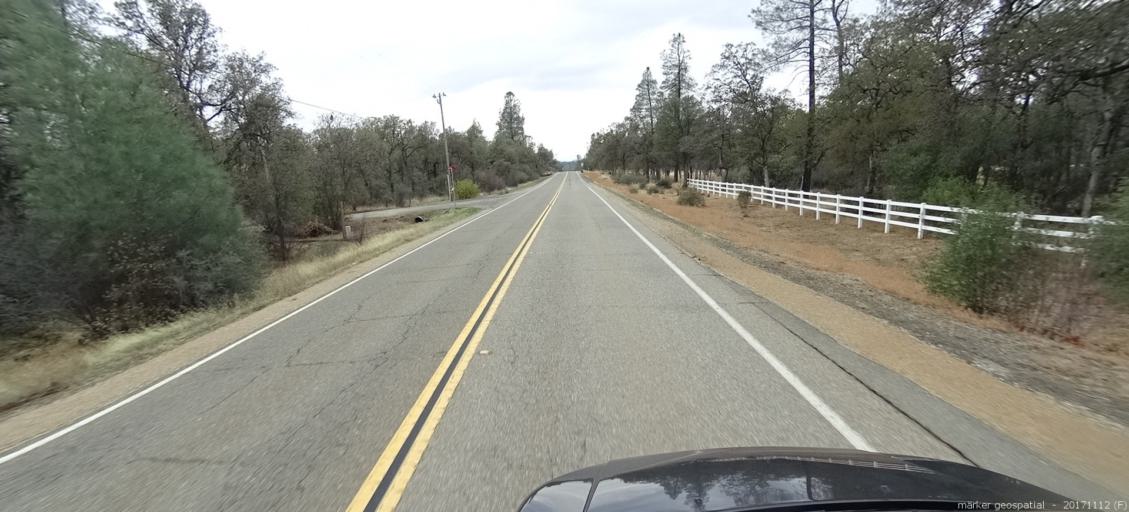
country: US
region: California
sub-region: Shasta County
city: Shingletown
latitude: 40.4996
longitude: -122.0413
